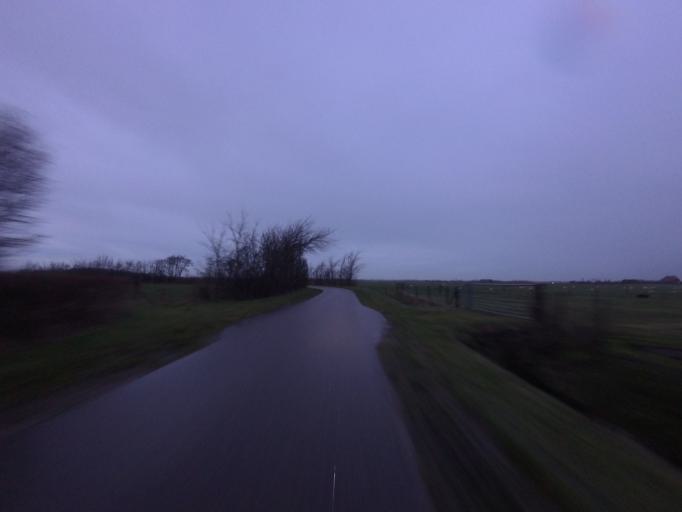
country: NL
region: North Holland
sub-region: Gemeente Texel
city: Den Burg
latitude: 53.0666
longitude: 4.8008
